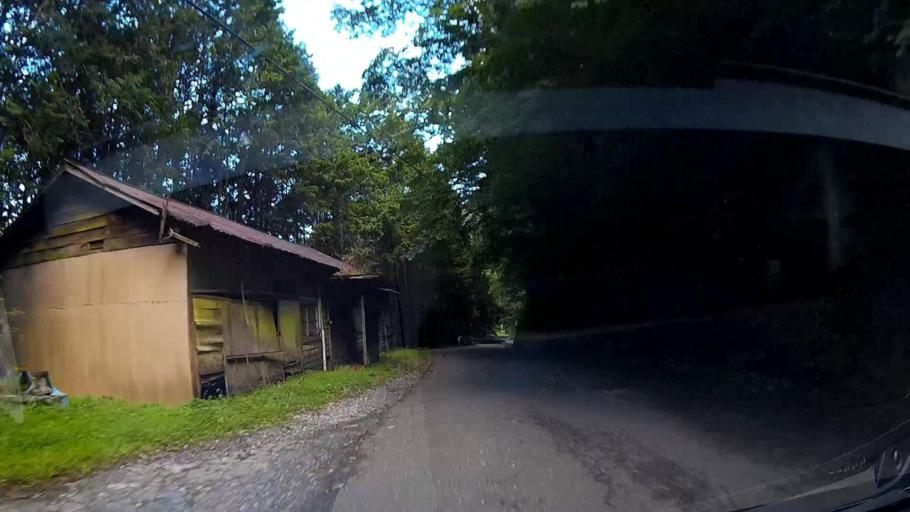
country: JP
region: Shizuoka
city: Shizuoka-shi
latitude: 35.2664
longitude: 138.2249
